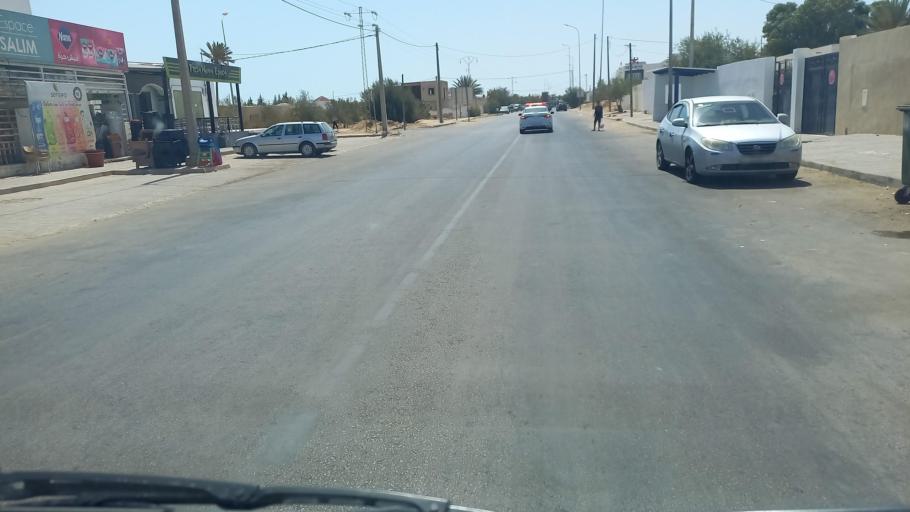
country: TN
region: Madanin
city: Houmt Souk
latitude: 33.7992
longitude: 10.8841
